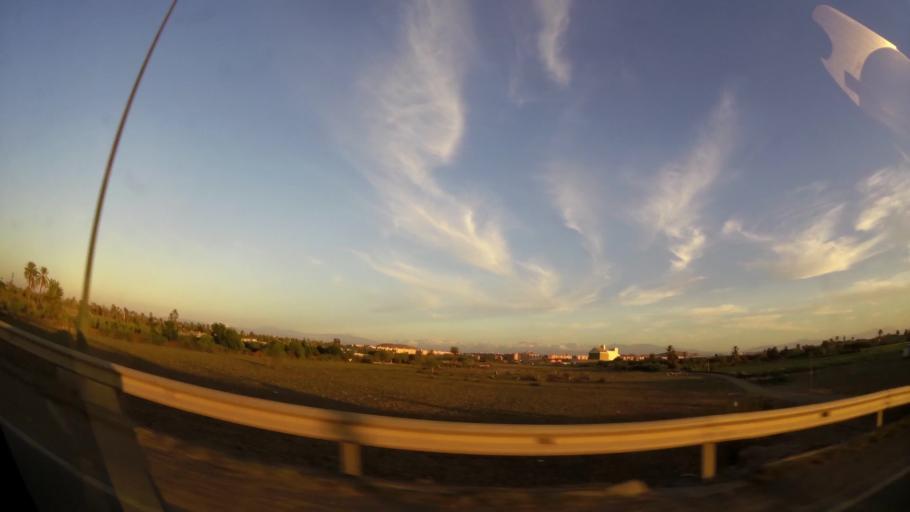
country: MA
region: Marrakech-Tensift-Al Haouz
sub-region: Marrakech
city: Marrakesh
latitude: 31.6879
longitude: -8.0318
